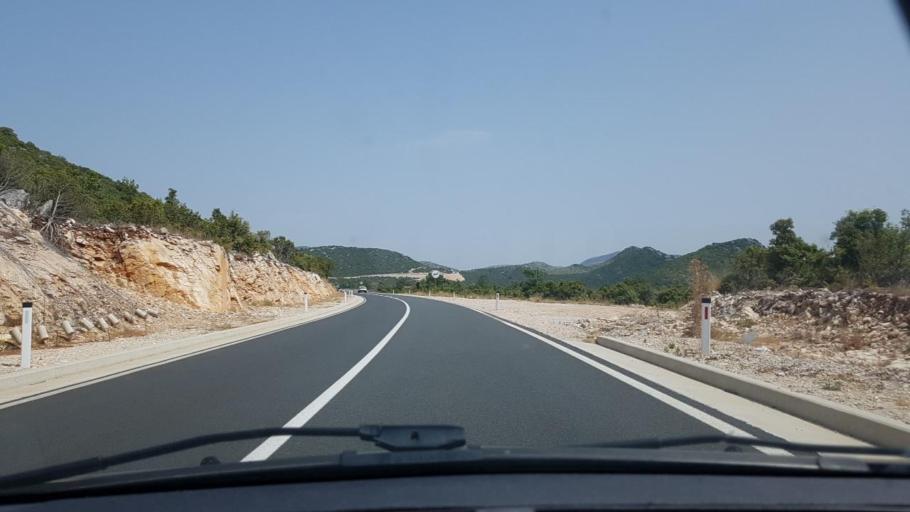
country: HR
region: Dubrovacko-Neretvanska
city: Ston
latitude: 42.9536
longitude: 17.7379
